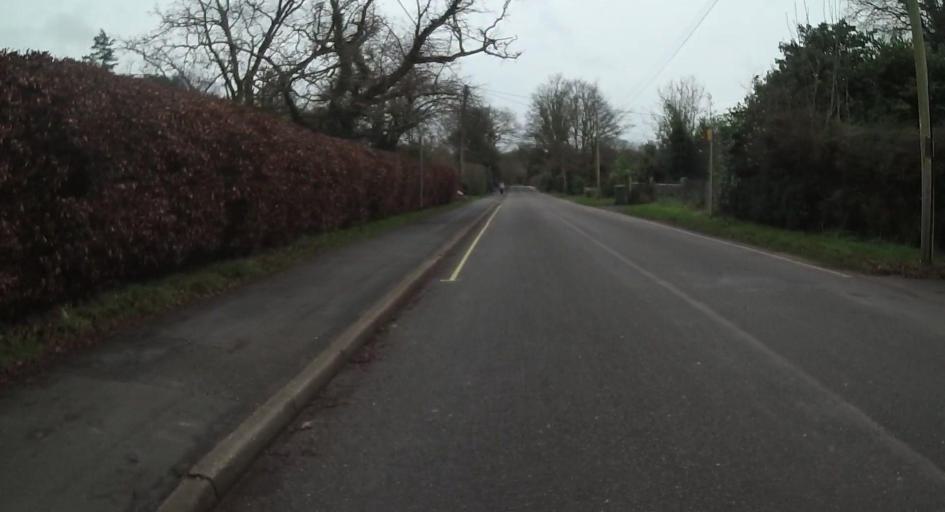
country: GB
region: England
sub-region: Hampshire
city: Four Marks
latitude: 51.1005
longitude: -1.0484
